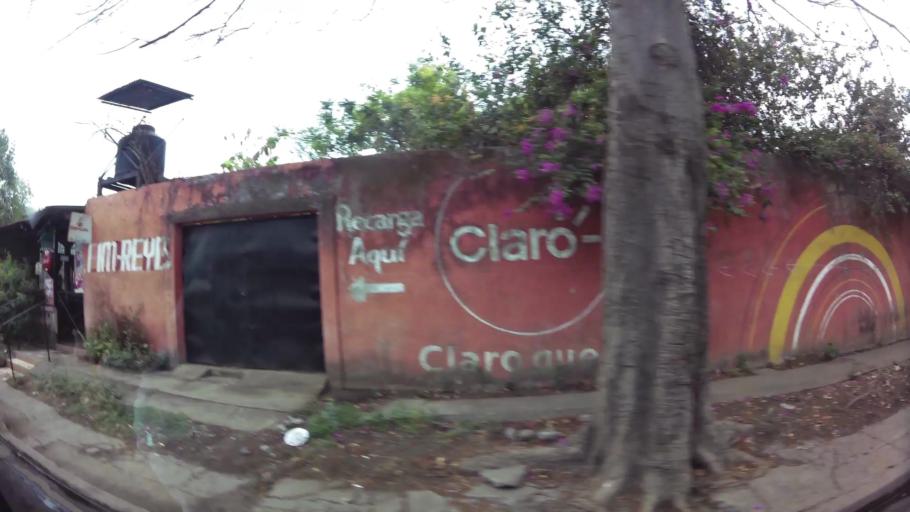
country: NI
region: Chinandega
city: Chinandega
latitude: 12.6171
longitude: -87.1168
